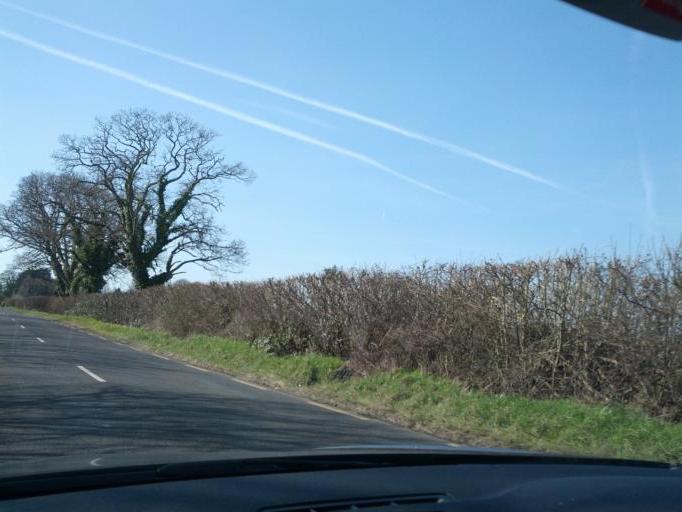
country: IE
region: Leinster
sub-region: Kildare
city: Leixlip
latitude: 53.3506
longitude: -6.4860
